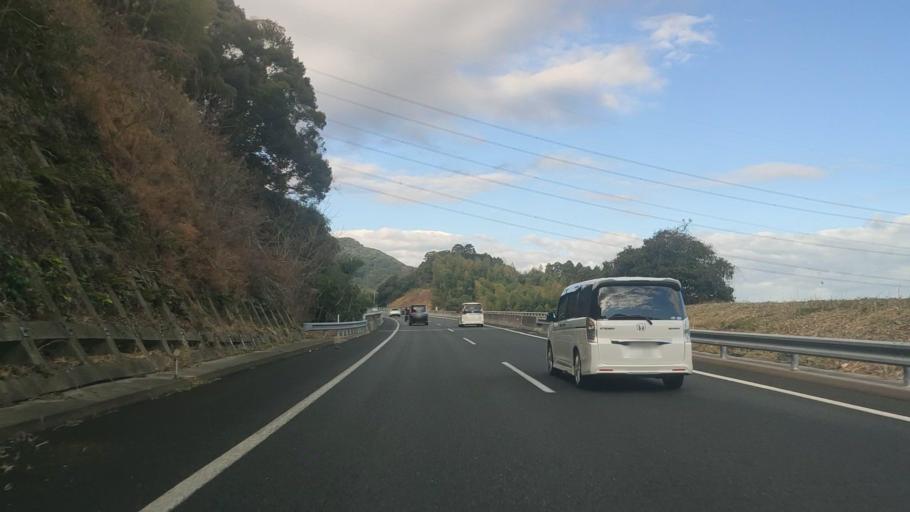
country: JP
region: Fukuoka
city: Kitakyushu
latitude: 33.8139
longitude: 130.9055
